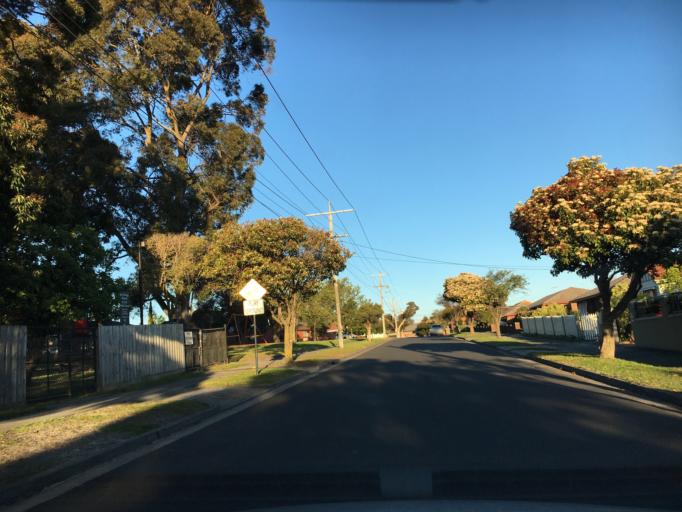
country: AU
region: Victoria
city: Clayton
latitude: -37.9065
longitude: 145.1116
